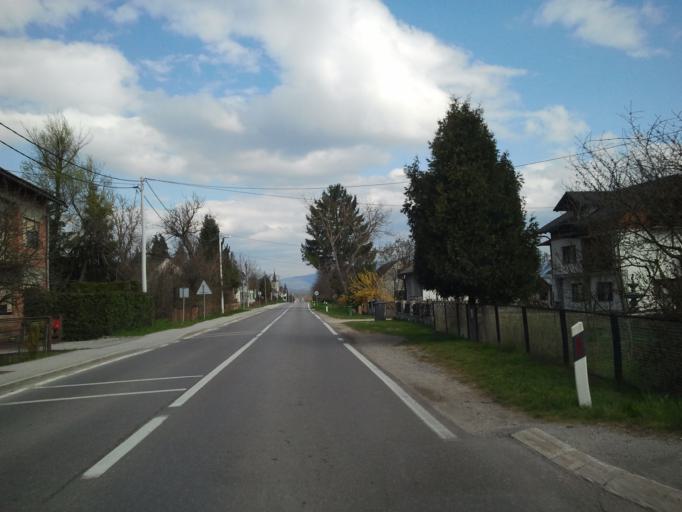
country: HR
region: Zagrebacka
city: Jastrebarsko
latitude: 45.6034
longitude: 15.5983
